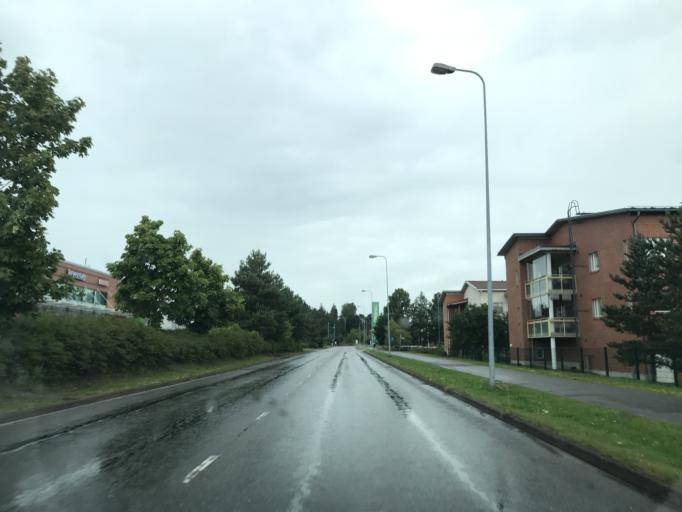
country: FI
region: Uusimaa
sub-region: Helsinki
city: Vihti
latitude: 60.3302
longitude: 24.3211
